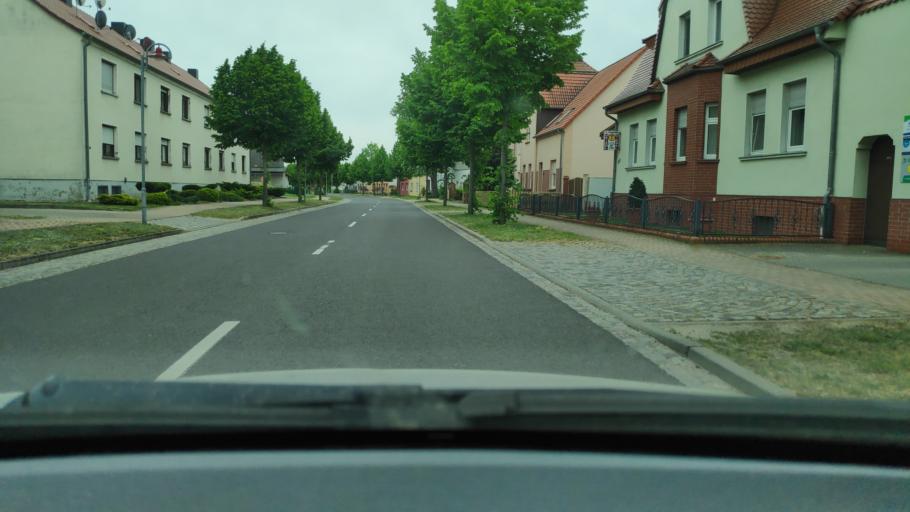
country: DE
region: Saxony-Anhalt
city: Leitzkau
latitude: 51.9915
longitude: 11.9868
